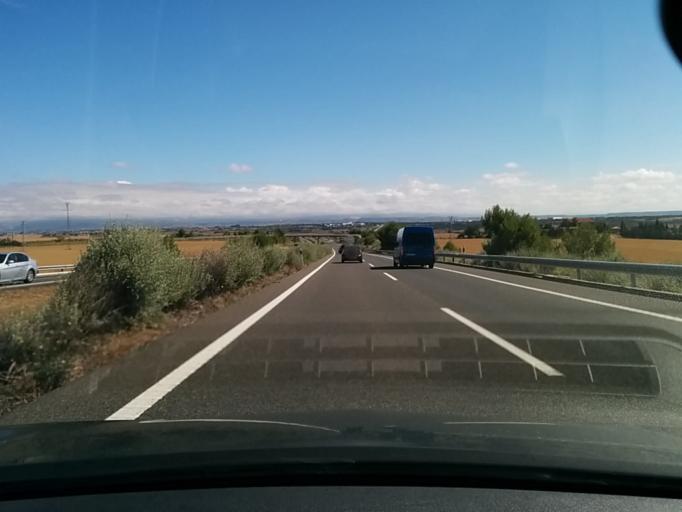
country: ES
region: Aragon
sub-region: Provincia de Huesca
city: Alerre
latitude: 42.0849
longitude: -0.4850
